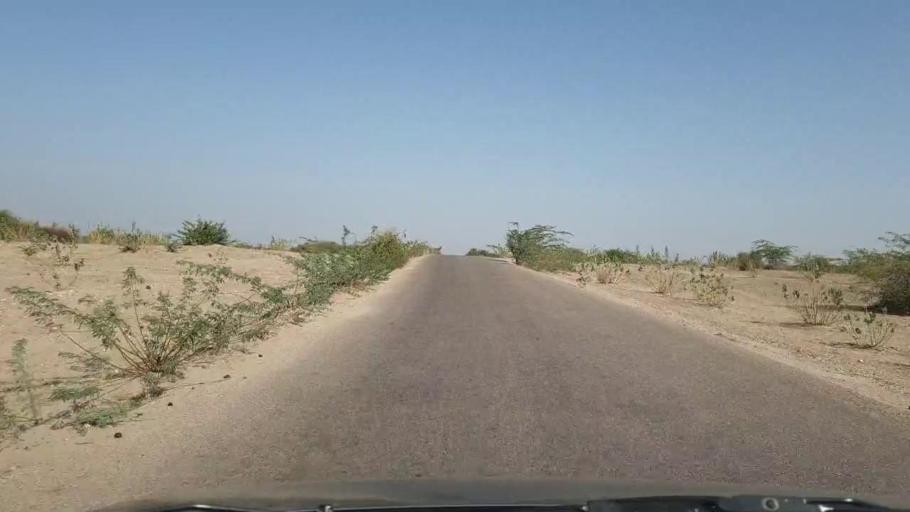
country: PK
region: Sindh
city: Chor
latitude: 25.5117
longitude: 69.8188
